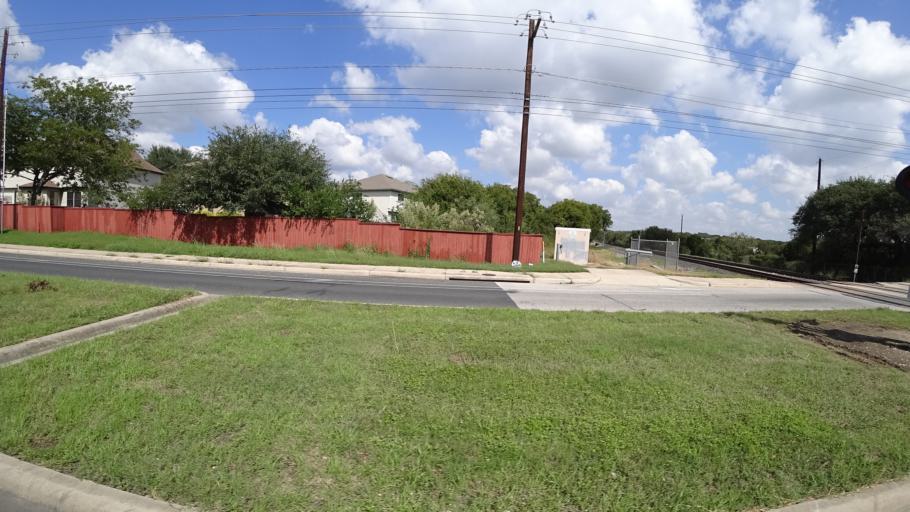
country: US
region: Texas
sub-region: Travis County
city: Manchaca
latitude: 30.1856
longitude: -97.8131
